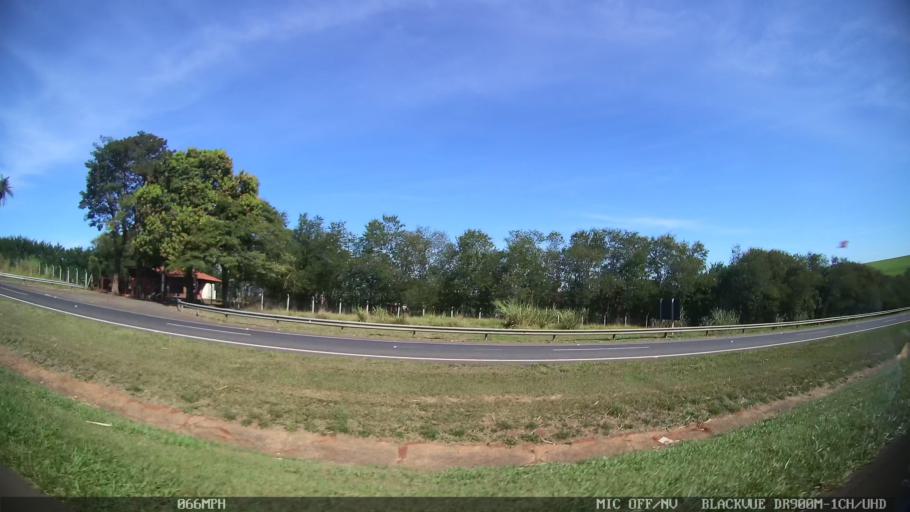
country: BR
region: Sao Paulo
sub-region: Porto Ferreira
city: Porto Ferreira
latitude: -21.8049
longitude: -47.5033
